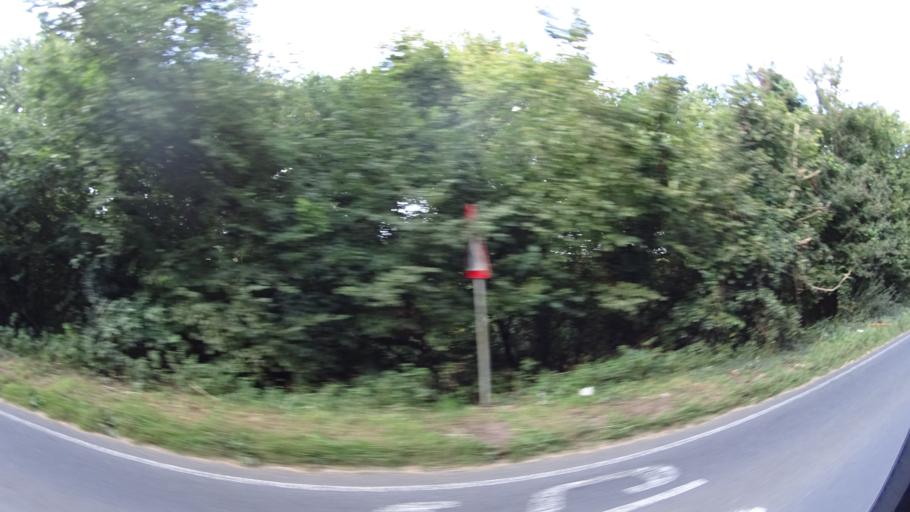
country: GB
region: England
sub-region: Dorset
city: Lytchett Matravers
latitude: 50.7677
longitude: -2.0635
